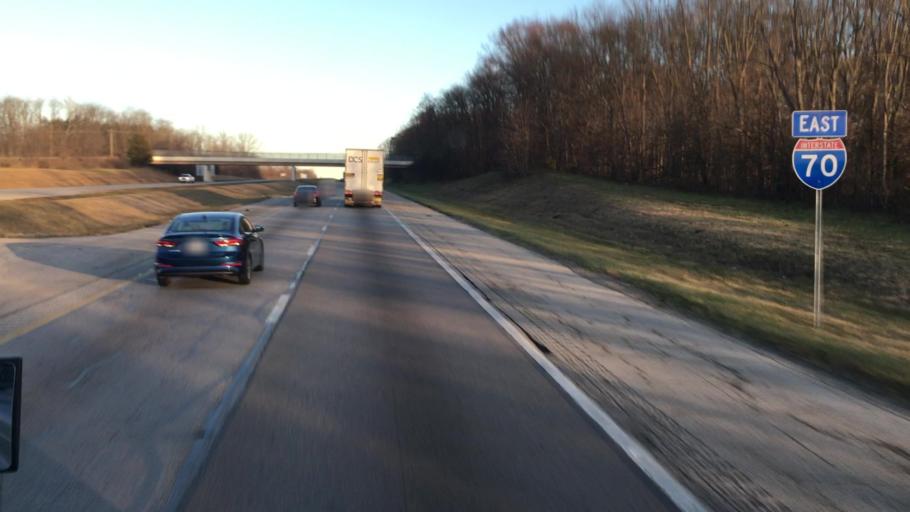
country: US
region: Ohio
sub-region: Preble County
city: Lewisburg
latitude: 39.8373
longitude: -84.5294
